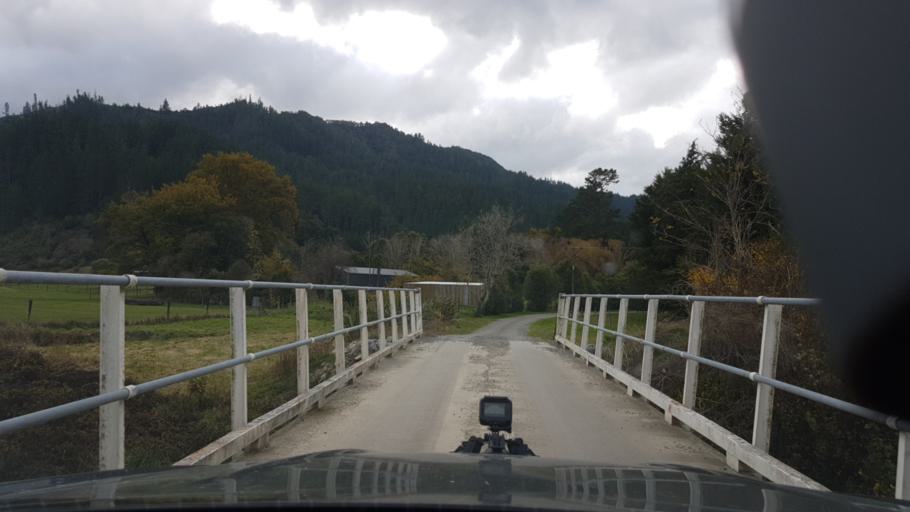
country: NZ
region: Marlborough
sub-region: Marlborough District
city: Blenheim
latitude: -41.4745
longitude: 173.7410
